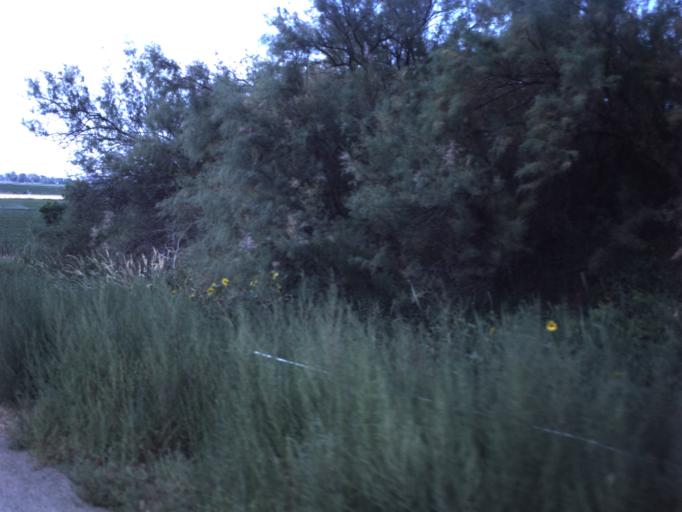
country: US
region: Utah
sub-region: Uintah County
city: Naples
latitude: 40.3877
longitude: -109.3460
